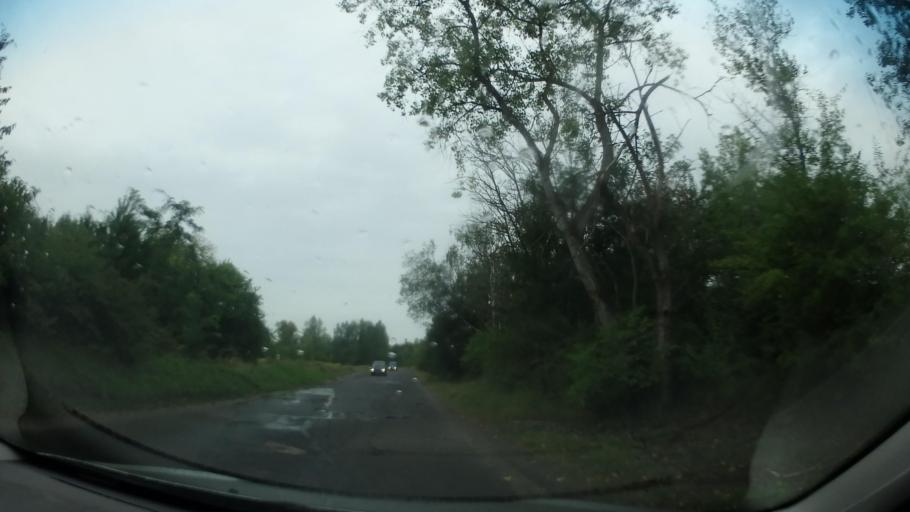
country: CZ
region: Central Bohemia
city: Milovice
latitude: 50.2425
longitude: 14.9156
